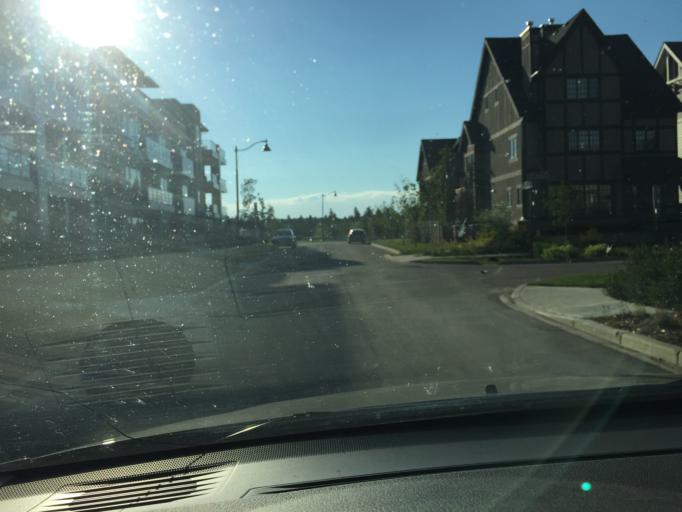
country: CA
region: Alberta
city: Calgary
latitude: 51.0164
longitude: -114.1320
